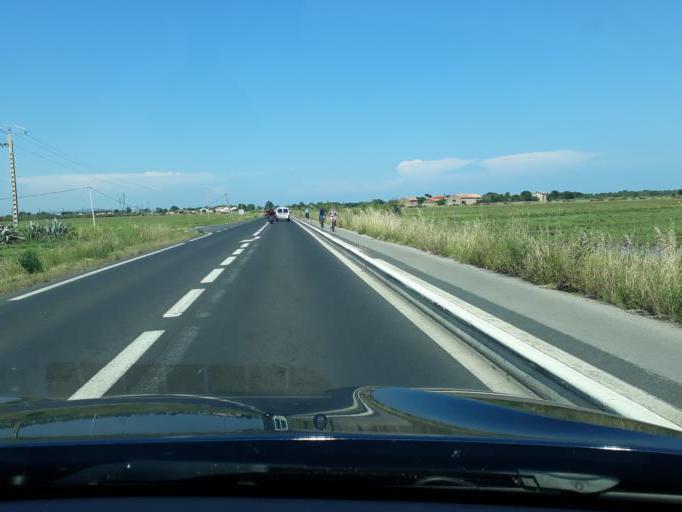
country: FR
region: Languedoc-Roussillon
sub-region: Departement de l'Herault
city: Le Cap d'Agde
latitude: 43.3113
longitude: 3.5207
